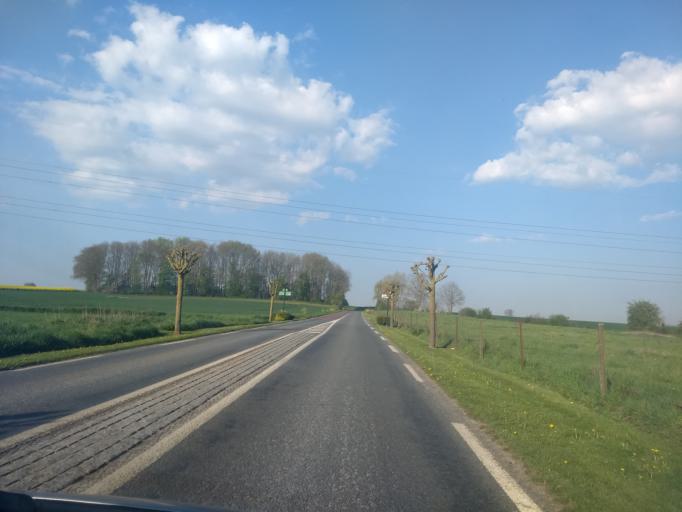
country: FR
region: Nord-Pas-de-Calais
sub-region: Departement du Pas-de-Calais
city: Bucquoy
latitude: 50.1124
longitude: 2.6897
